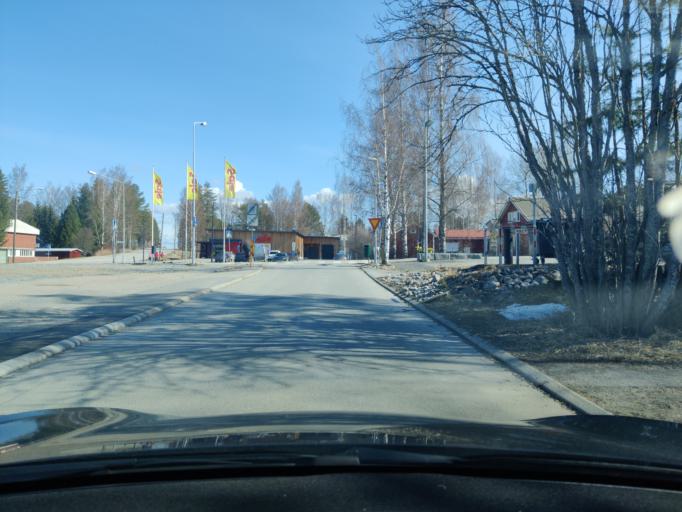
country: FI
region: Northern Savo
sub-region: Kuopio
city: Vehmersalmi
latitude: 62.7607
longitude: 28.0288
